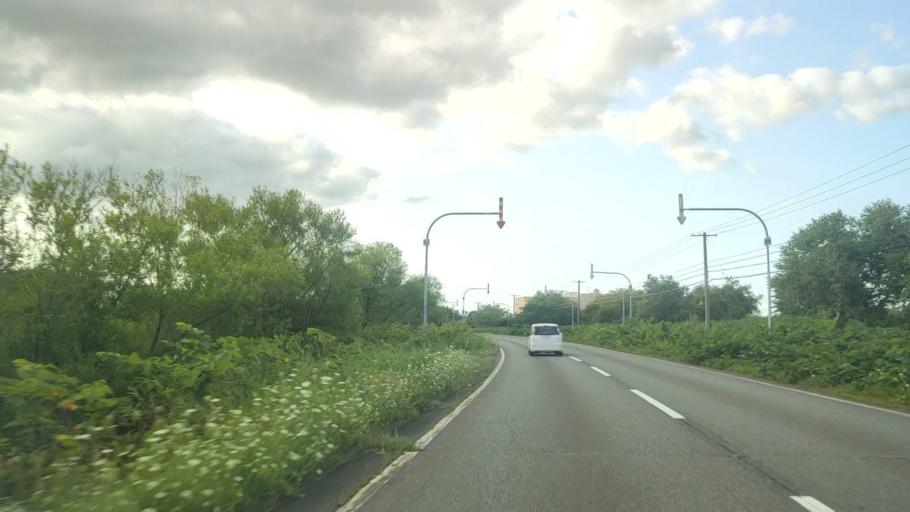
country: JP
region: Hokkaido
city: Makubetsu
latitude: 45.0006
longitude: 141.8165
